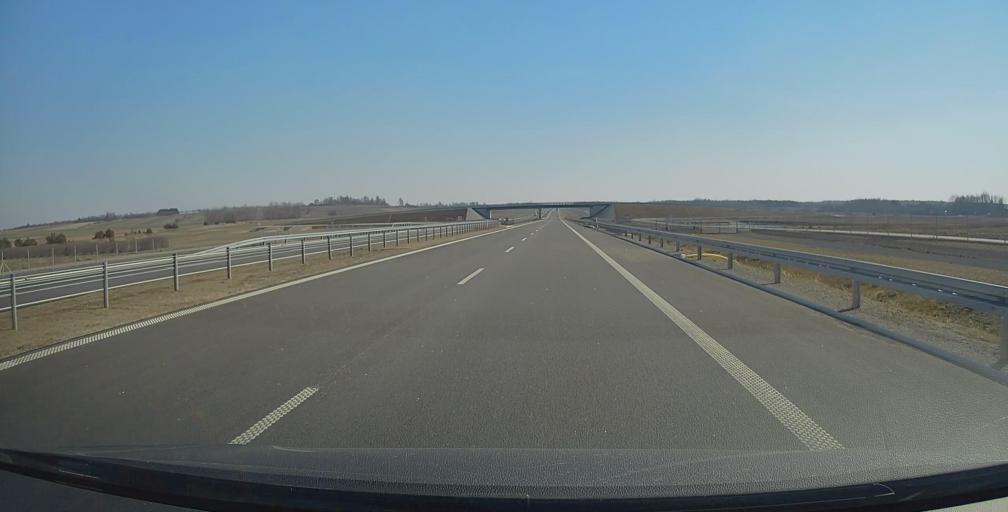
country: PL
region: Lublin Voivodeship
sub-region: Powiat janowski
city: Modliborzyce
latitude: 50.7419
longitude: 22.3126
